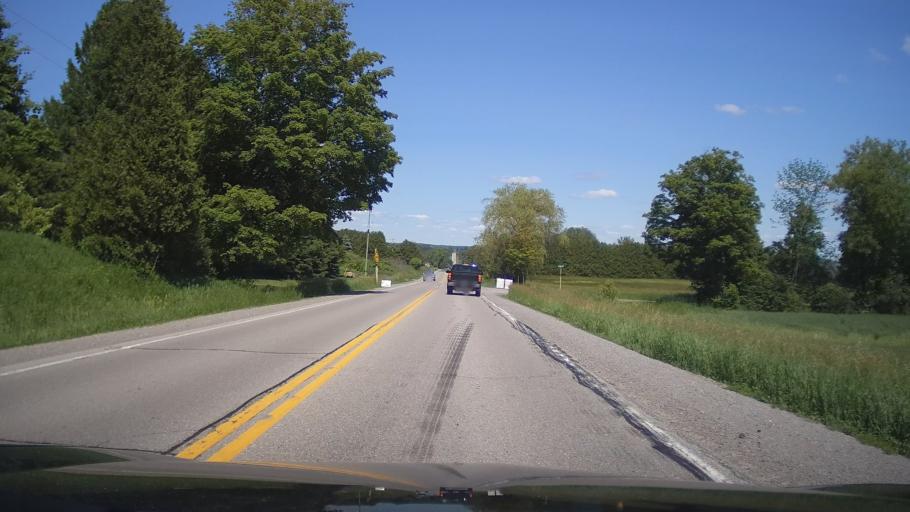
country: CA
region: Ontario
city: Oshawa
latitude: 44.0083
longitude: -78.7999
